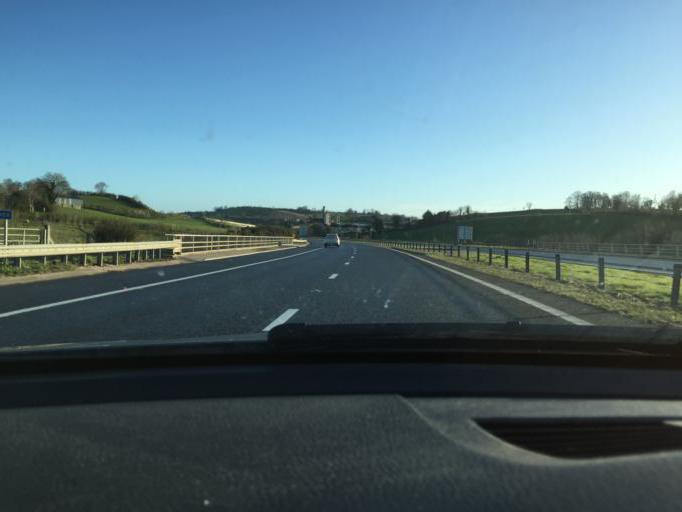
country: GB
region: Northern Ireland
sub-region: Newry and Mourne District
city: Newry
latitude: 54.2207
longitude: -6.3214
